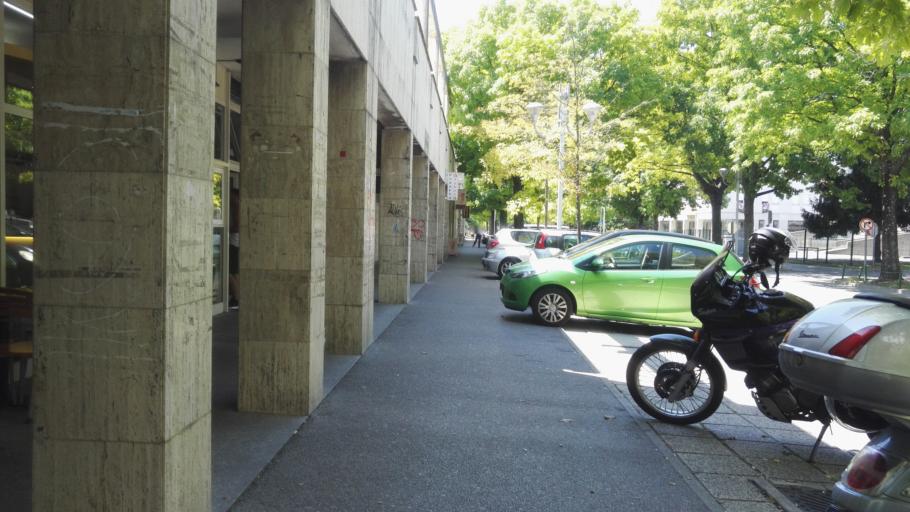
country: SI
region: Nova Gorica
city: Nova Gorica
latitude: 45.9581
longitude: 13.6428
